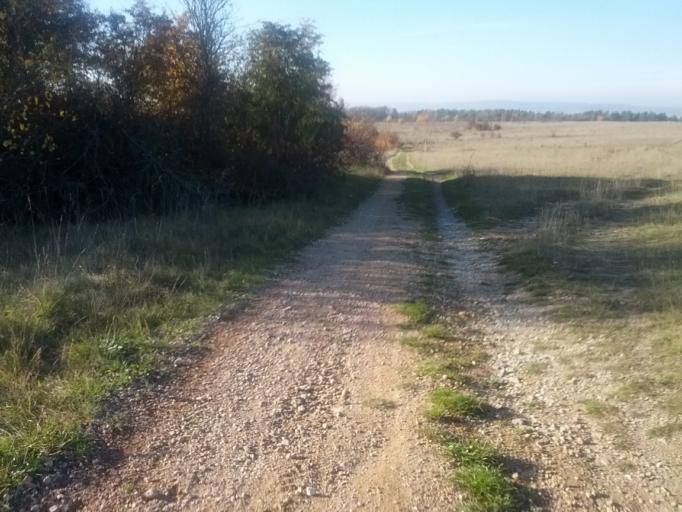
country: DE
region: Thuringia
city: Goldbach
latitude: 50.9593
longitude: 10.6337
